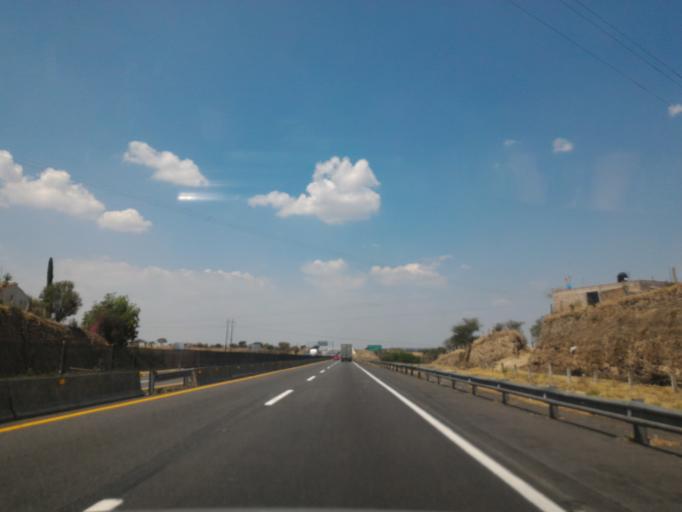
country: MX
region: Jalisco
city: Jalostotitlan
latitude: 21.1203
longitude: -102.4551
